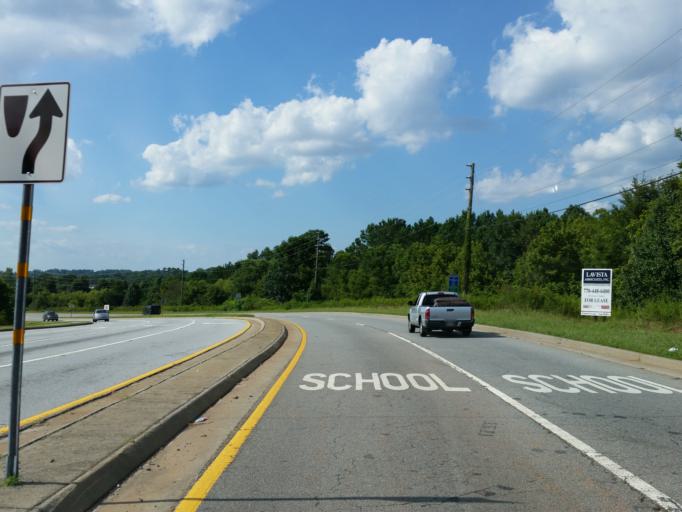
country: US
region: Georgia
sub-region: Gwinnett County
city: Lawrenceville
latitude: 33.9535
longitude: -84.0266
